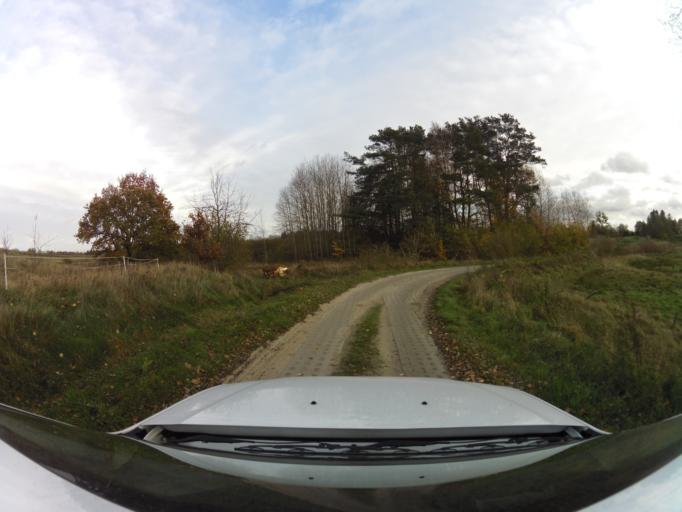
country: PL
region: West Pomeranian Voivodeship
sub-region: Powiat gryficki
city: Gryfice
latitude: 53.8198
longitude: 15.1272
